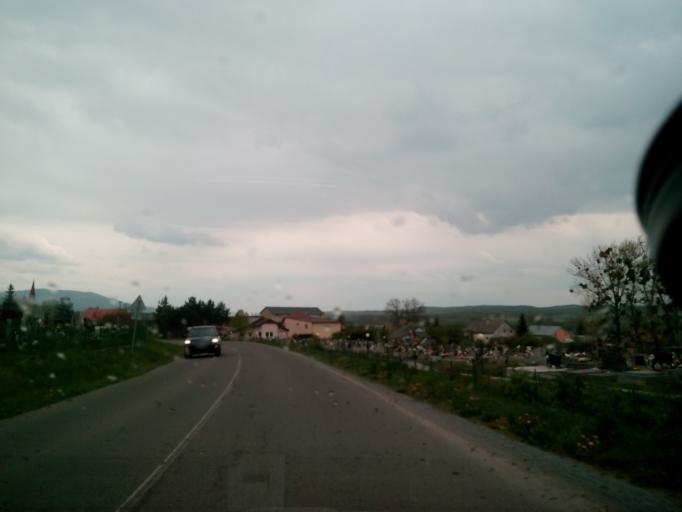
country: SK
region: Kosicky
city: Kosice
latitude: 48.7457
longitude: 21.4392
